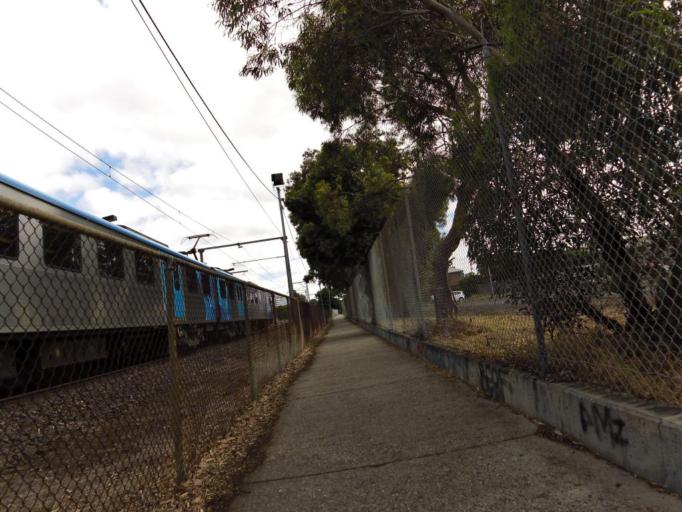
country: AU
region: Victoria
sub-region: Moreland
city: Coburg North
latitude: -37.7327
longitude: 144.9628
